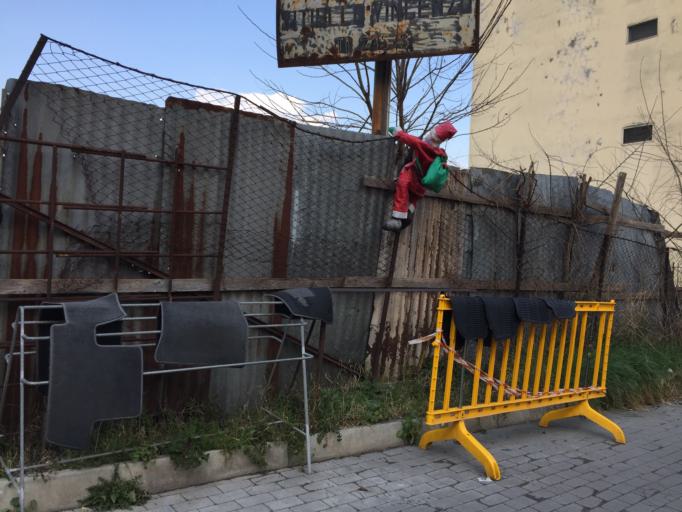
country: IT
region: Campania
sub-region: Provincia di Benevento
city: Benevento
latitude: 41.1345
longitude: 14.7830
